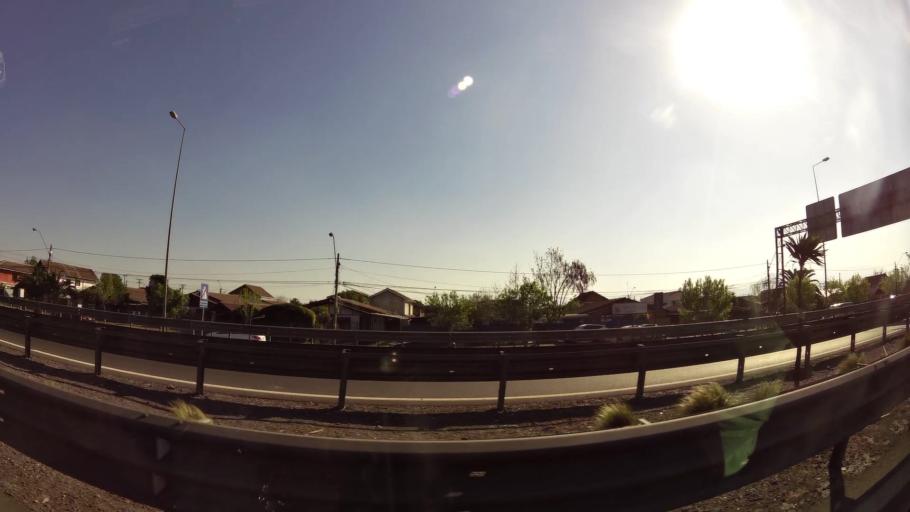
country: CL
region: Santiago Metropolitan
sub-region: Provincia de Santiago
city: Lo Prado
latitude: -33.4928
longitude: -70.7479
